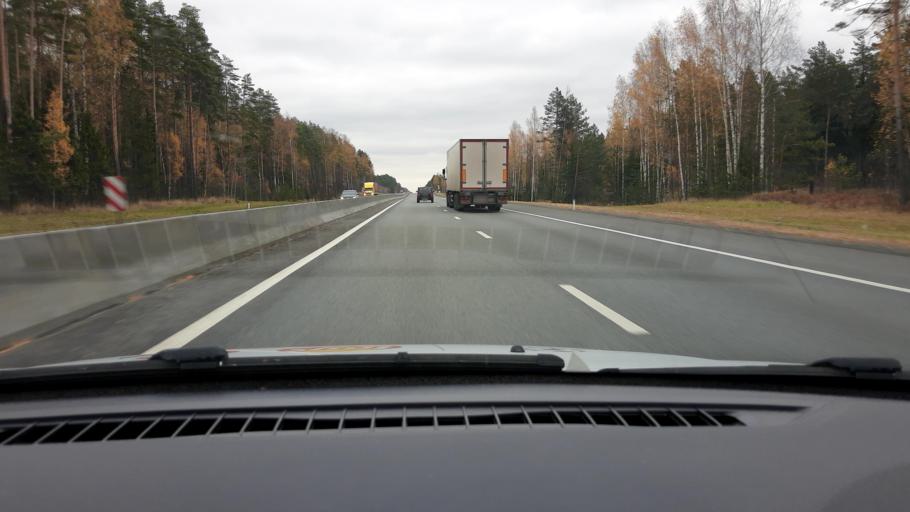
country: RU
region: Nizjnij Novgorod
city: Yuganets
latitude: 56.2869
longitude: 43.2067
